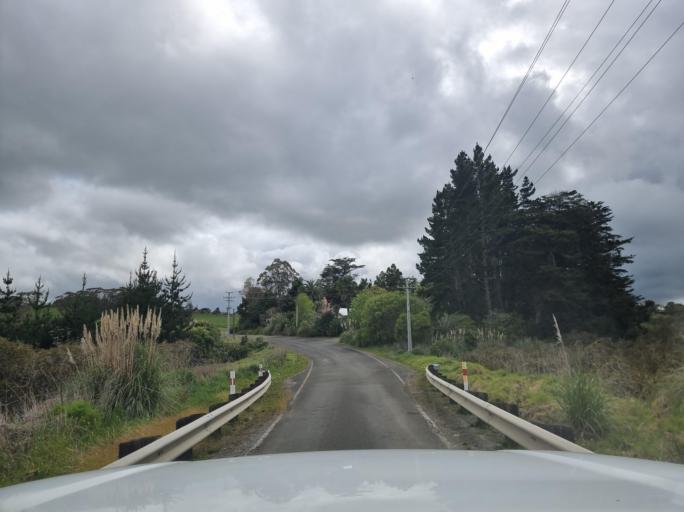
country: NZ
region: Northland
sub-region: Whangarei
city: Ruakaka
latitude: -36.1239
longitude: 174.1895
